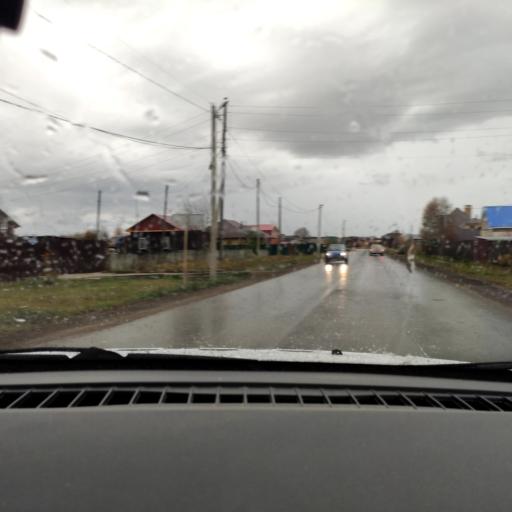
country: RU
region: Perm
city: Kultayevo
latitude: 57.8987
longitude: 55.9550
